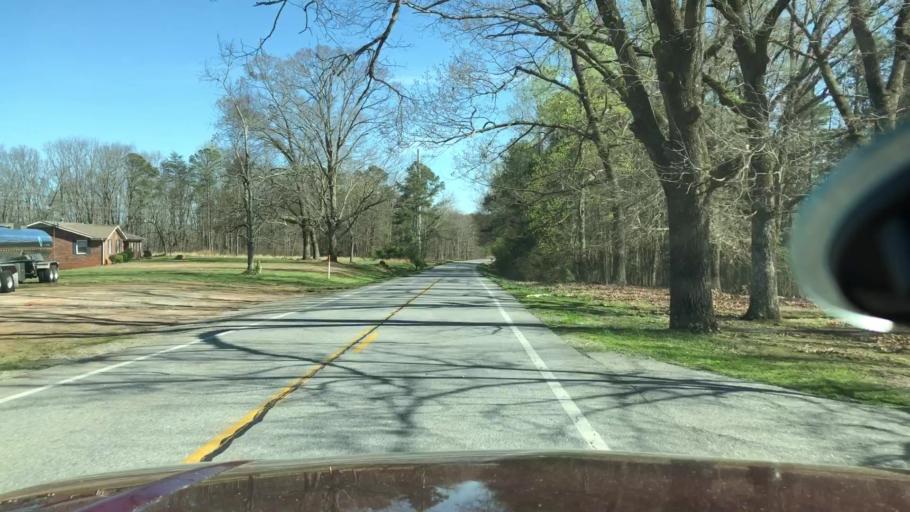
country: US
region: Georgia
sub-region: Dawson County
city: Dawsonville
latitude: 34.4646
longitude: -84.1764
